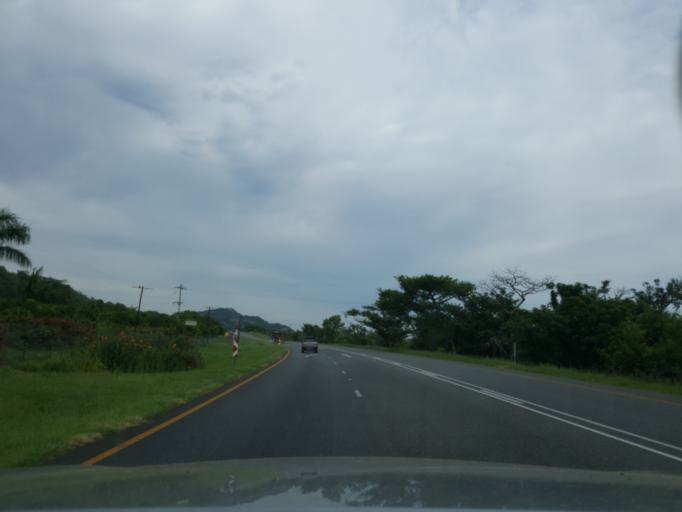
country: ZA
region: Mpumalanga
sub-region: Ehlanzeni District
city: Nelspruit
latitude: -25.4871
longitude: 31.1476
